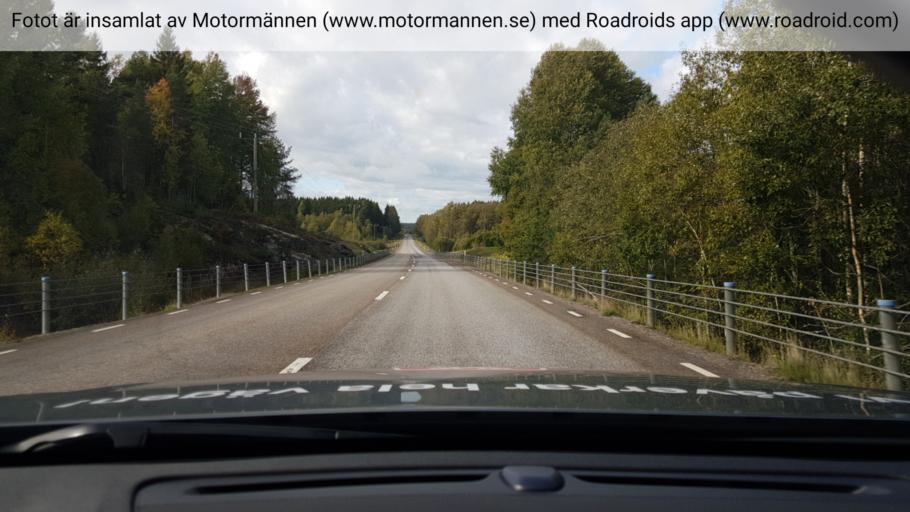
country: SE
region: Vaermland
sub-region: Arjangs Kommun
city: Arjaeng
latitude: 59.4600
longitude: 12.0277
